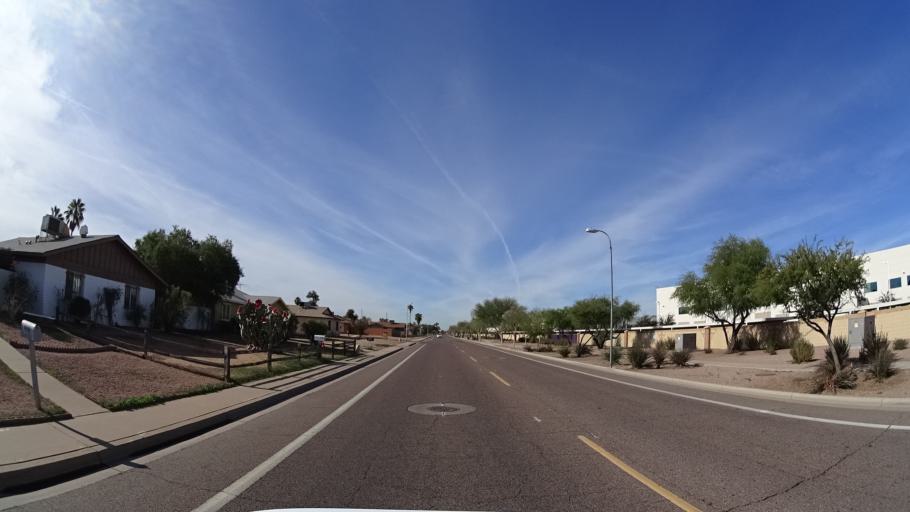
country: US
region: Arizona
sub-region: Maricopa County
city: Guadalupe
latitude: 33.3998
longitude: -111.9839
